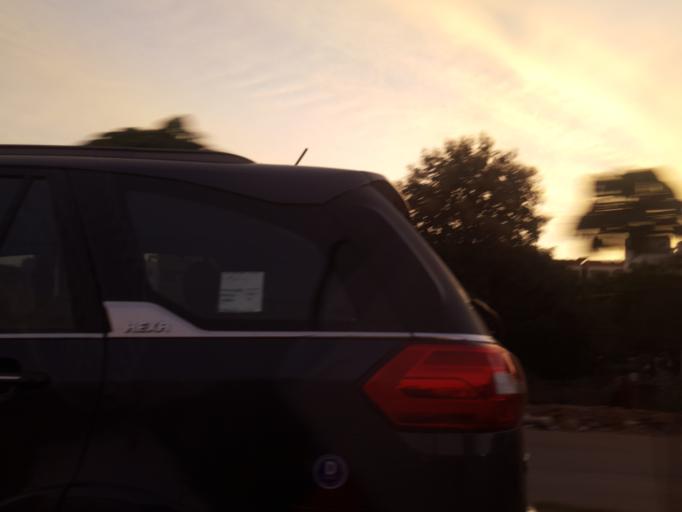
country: IN
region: Telangana
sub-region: Rangareddi
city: Kukatpalli
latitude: 17.5031
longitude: 78.3621
